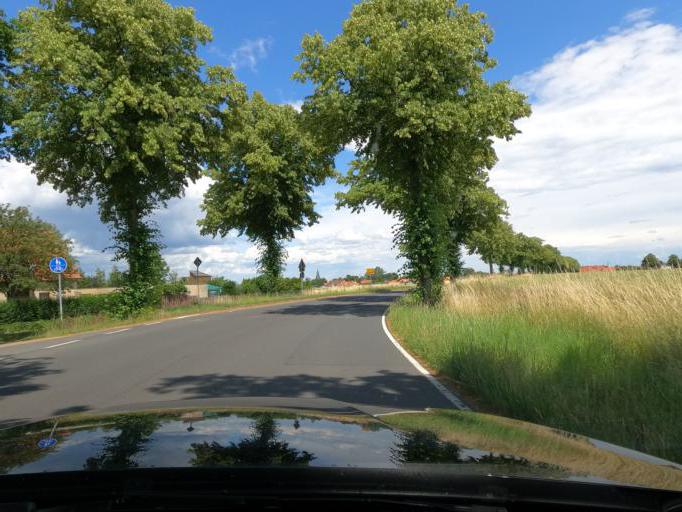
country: DE
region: Lower Saxony
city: Sohlde
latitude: 52.1832
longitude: 10.1933
